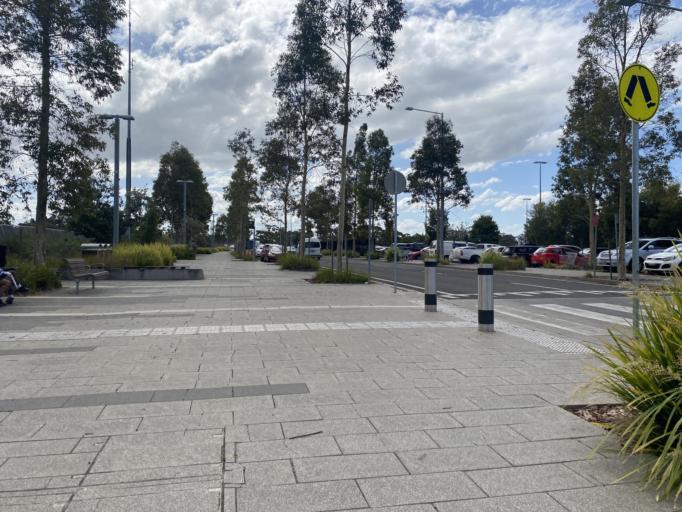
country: AU
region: New South Wales
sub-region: Campbelltown Municipality
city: Denham Court
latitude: -33.9690
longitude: 150.8586
